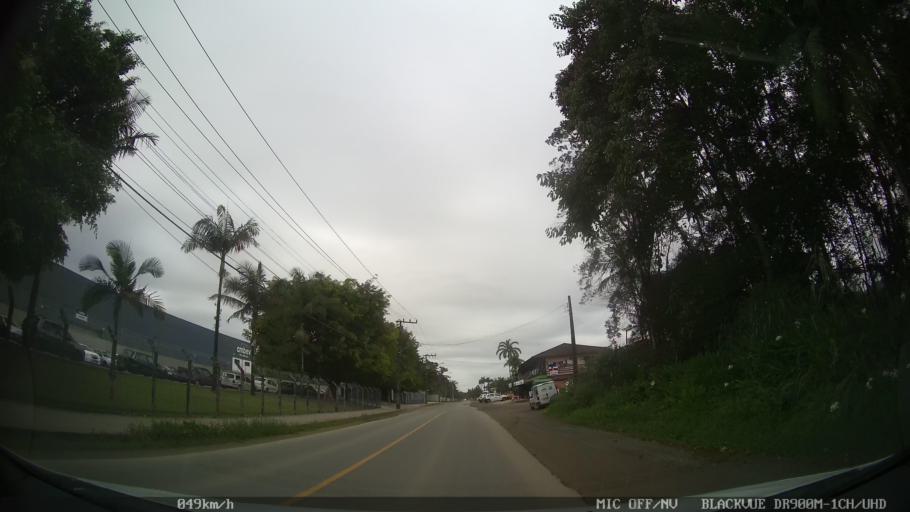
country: BR
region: Santa Catarina
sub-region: Joinville
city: Joinville
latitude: -26.2617
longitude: -48.9246
